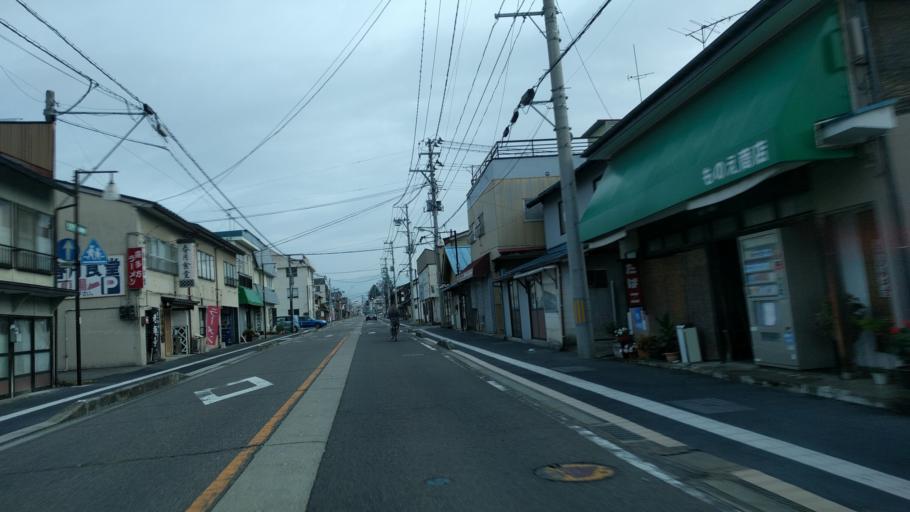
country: JP
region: Fukushima
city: Kitakata
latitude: 37.6486
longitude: 139.8688
